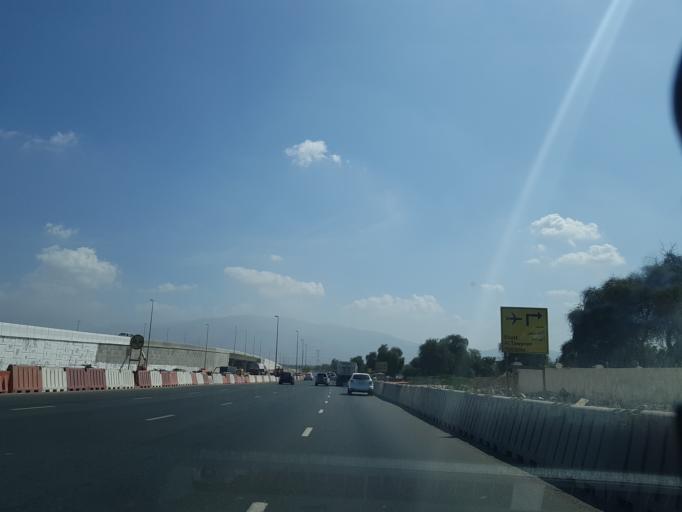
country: AE
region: Ra's al Khaymah
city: Ras al-Khaimah
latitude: 25.7004
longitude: 55.9643
